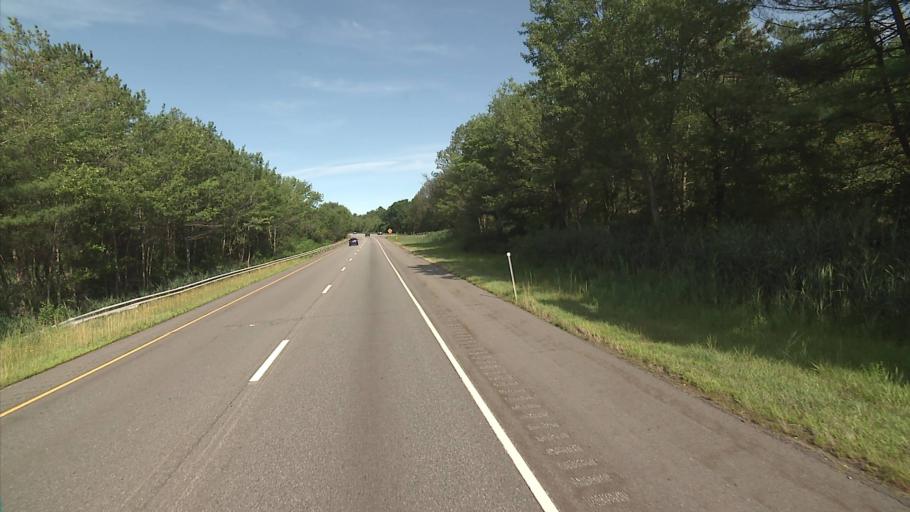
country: US
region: Connecticut
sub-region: New London County
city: Colchester
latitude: 41.5712
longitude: -72.3397
